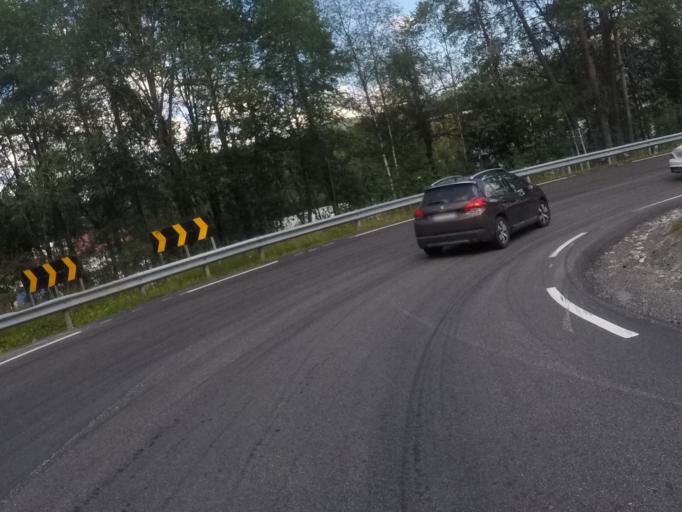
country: NO
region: Sogn og Fjordane
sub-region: Forde
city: Forde
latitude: 61.4456
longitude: 5.8181
